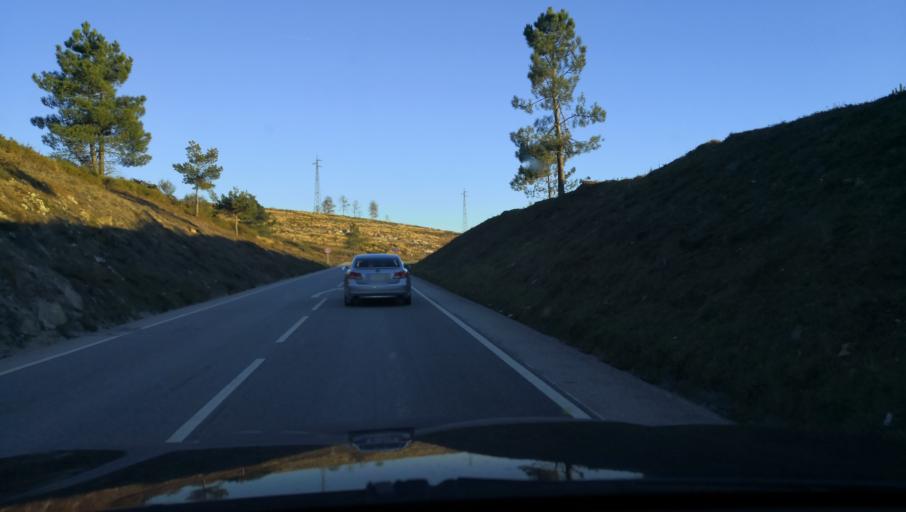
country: PT
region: Vila Real
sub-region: Ribeira de Pena
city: Ribeira de Pena
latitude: 41.4996
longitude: -7.7333
